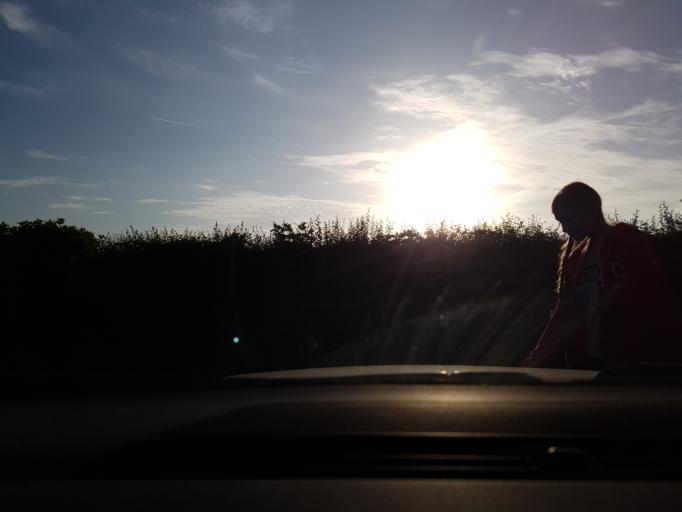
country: GB
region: England
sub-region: Northamptonshire
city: Deanshanger
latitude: 52.0504
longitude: -0.9129
